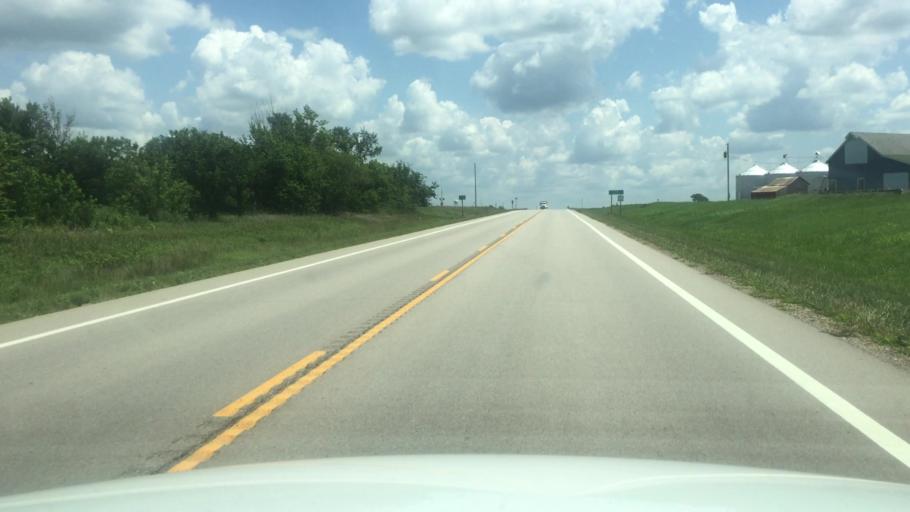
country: US
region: Kansas
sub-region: Brown County
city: Horton
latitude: 39.6533
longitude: -95.3649
